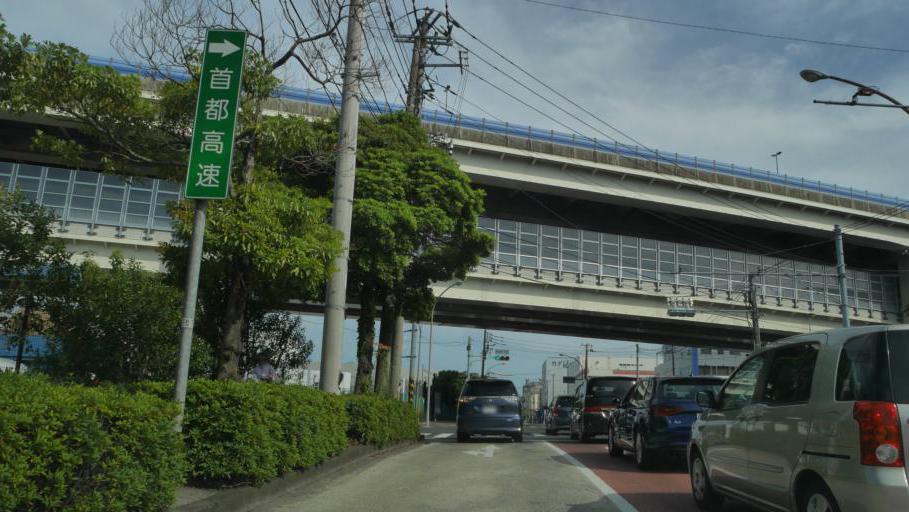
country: JP
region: Kanagawa
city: Yokohama
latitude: 35.4113
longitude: 139.6261
